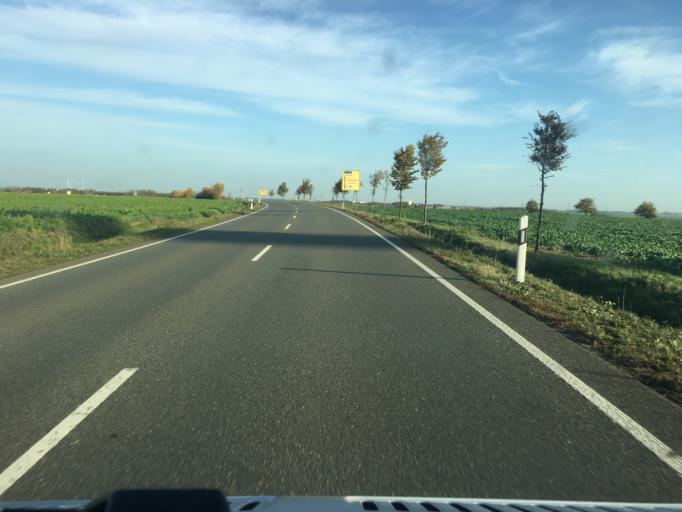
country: DE
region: Thuringia
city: Heyersdorf
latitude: 50.8345
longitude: 12.3403
